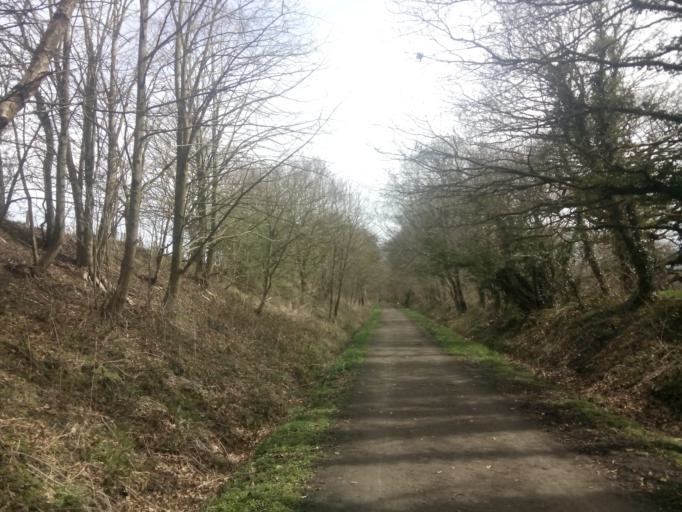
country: GB
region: England
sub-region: County Durham
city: Ushaw Moor
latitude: 54.7692
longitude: -1.6270
